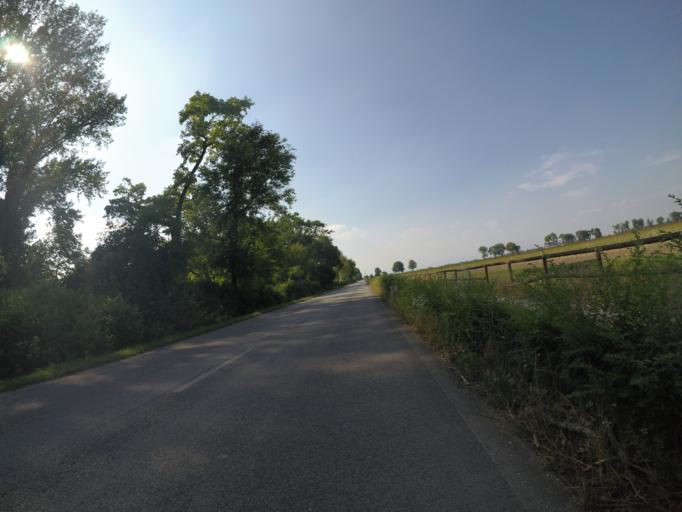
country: IT
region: Friuli Venezia Giulia
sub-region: Provincia di Udine
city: Camino al Tagliamento
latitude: 45.9279
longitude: 12.9612
